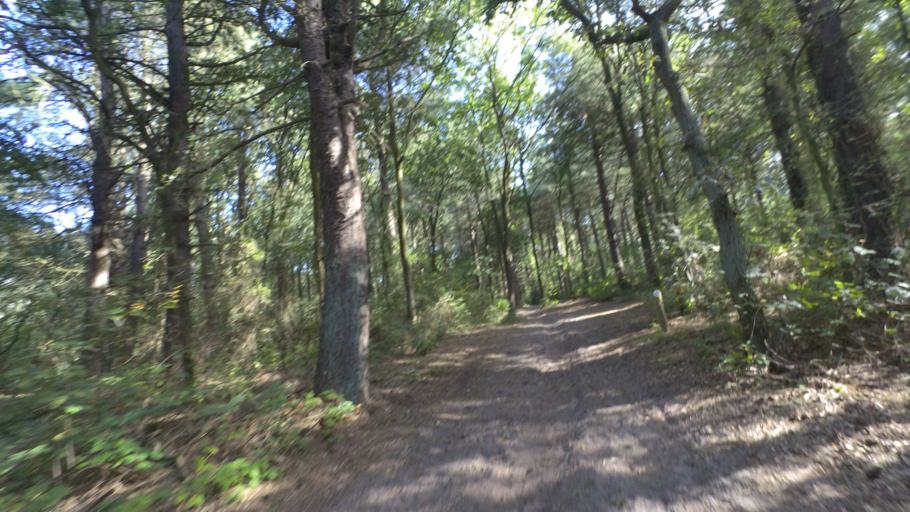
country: NL
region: Friesland
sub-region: Gemeente Ameland
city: Hollum
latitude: 53.4484
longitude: 5.7015
